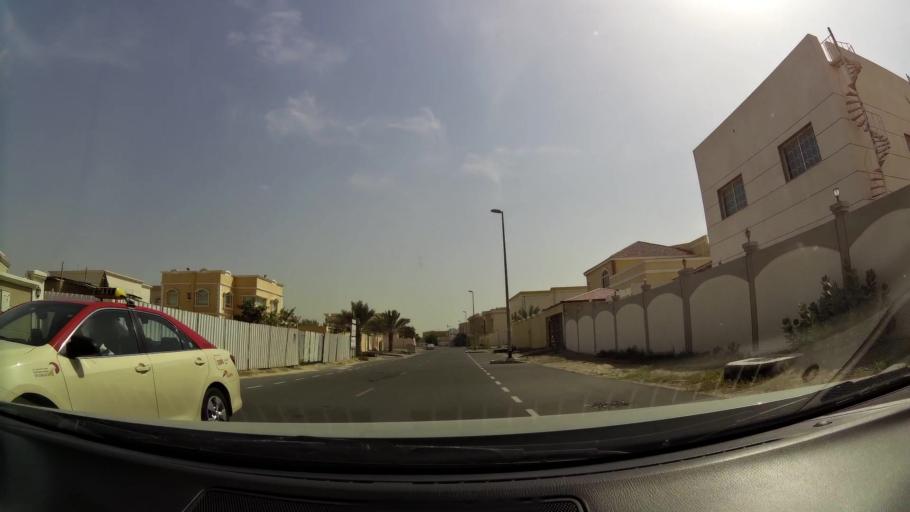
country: AE
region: Ash Shariqah
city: Sharjah
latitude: 25.1978
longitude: 55.4034
